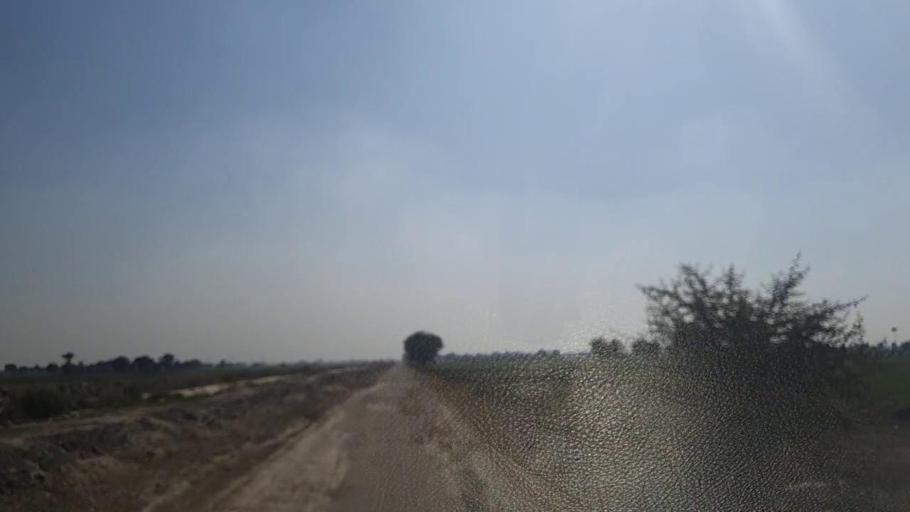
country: PK
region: Sindh
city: Shahpur Chakar
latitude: 26.2128
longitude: 68.5839
